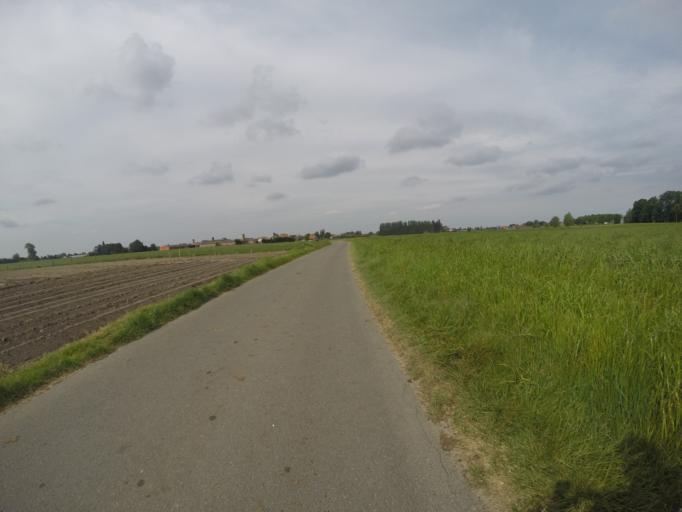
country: BE
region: Flanders
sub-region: Provincie West-Vlaanderen
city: Wingene
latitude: 51.0650
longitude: 3.3295
